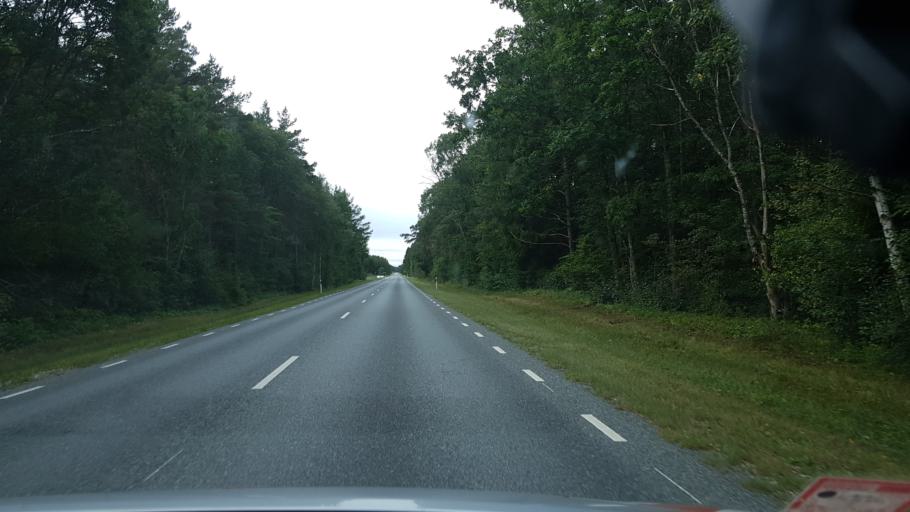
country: EE
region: Saare
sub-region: Kuressaare linn
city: Kuressaare
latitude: 58.3604
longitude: 22.6078
